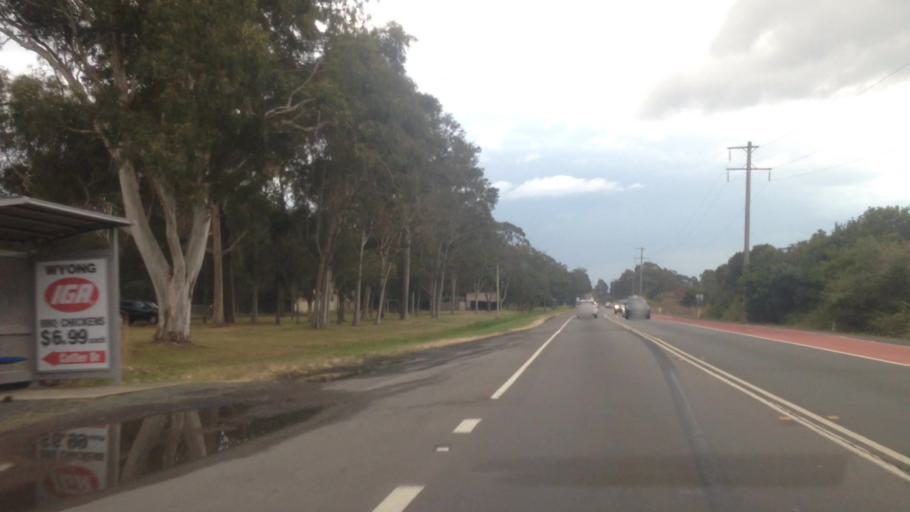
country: AU
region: New South Wales
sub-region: Wyong Shire
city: Chittaway Bay
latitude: -33.2802
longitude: 151.4268
